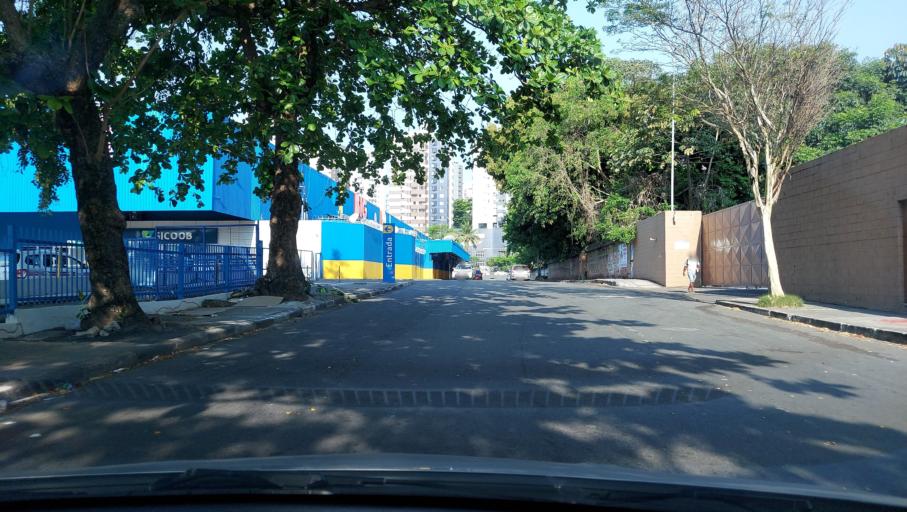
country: BR
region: Bahia
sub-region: Salvador
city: Salvador
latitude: -12.9860
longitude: -38.4658
